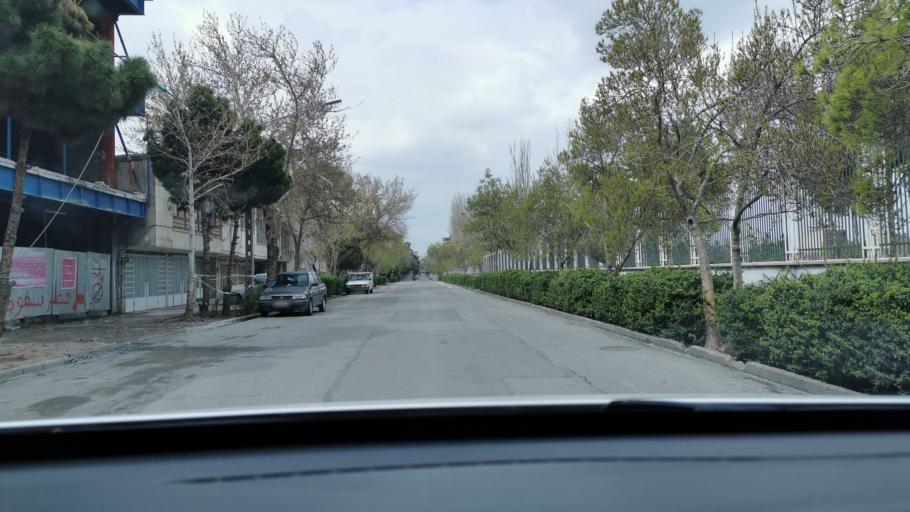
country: IR
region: Razavi Khorasan
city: Mashhad
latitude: 36.2855
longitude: 59.5792
